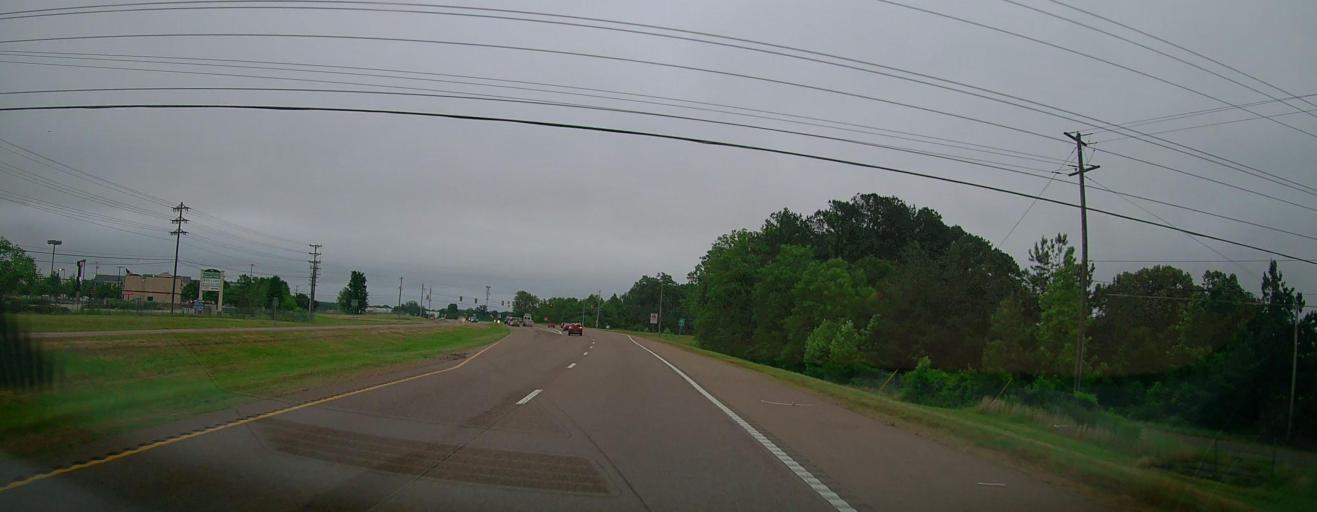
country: US
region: Mississippi
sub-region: De Soto County
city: Olive Branch
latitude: 34.9630
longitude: -89.7984
